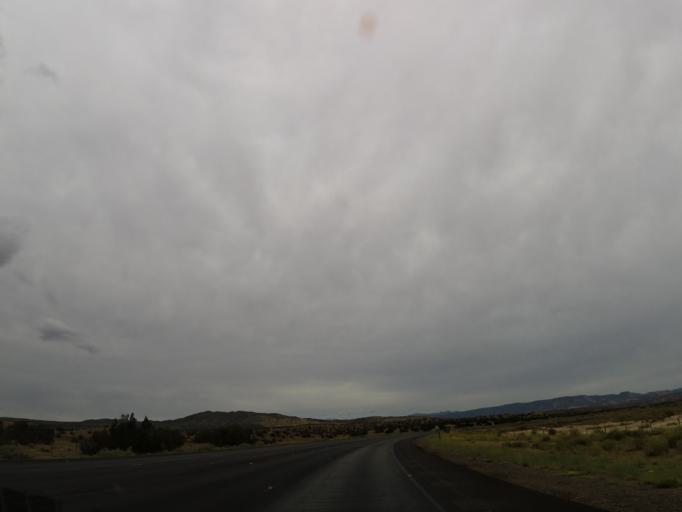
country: US
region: New Mexico
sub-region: Sandoval County
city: Jemez Pueblo
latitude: 35.5514
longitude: -106.8210
